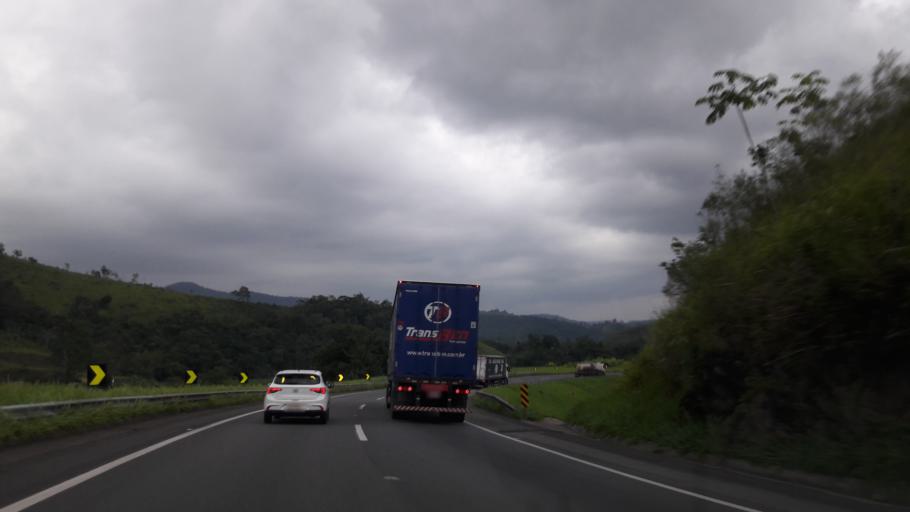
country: BR
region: Sao Paulo
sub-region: Cajati
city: Cajati
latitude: -24.8202
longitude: -48.2113
